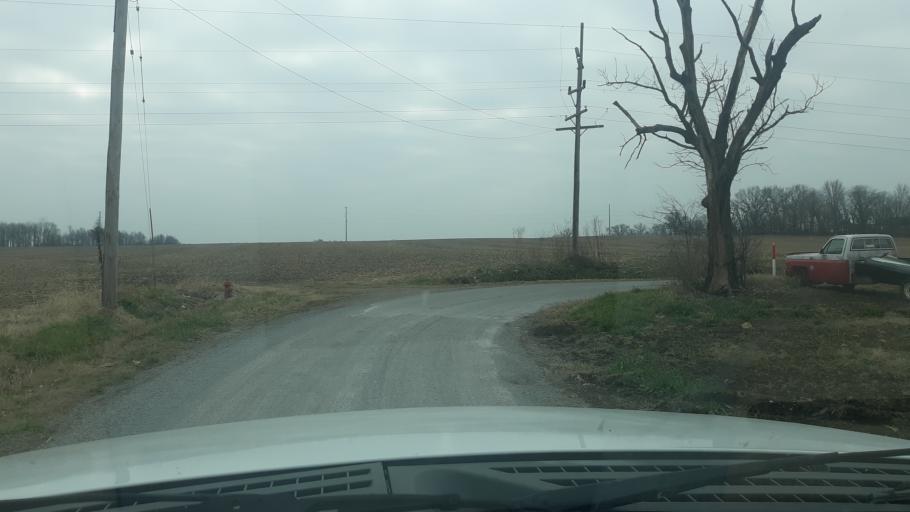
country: US
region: Illinois
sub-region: Saline County
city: Harrisburg
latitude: 37.8344
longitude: -88.6121
